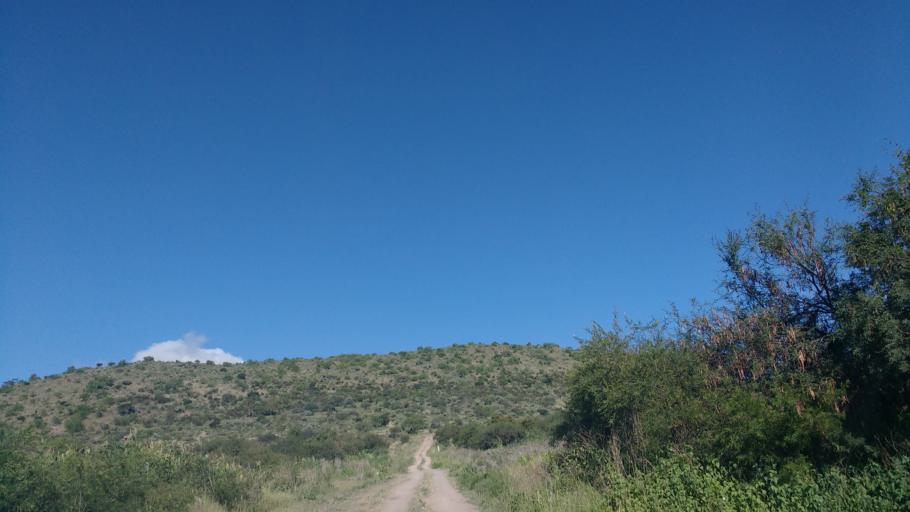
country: MX
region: Hidalgo
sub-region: Tezontepec de Aldama
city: Tenango
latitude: 20.2472
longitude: -99.2760
